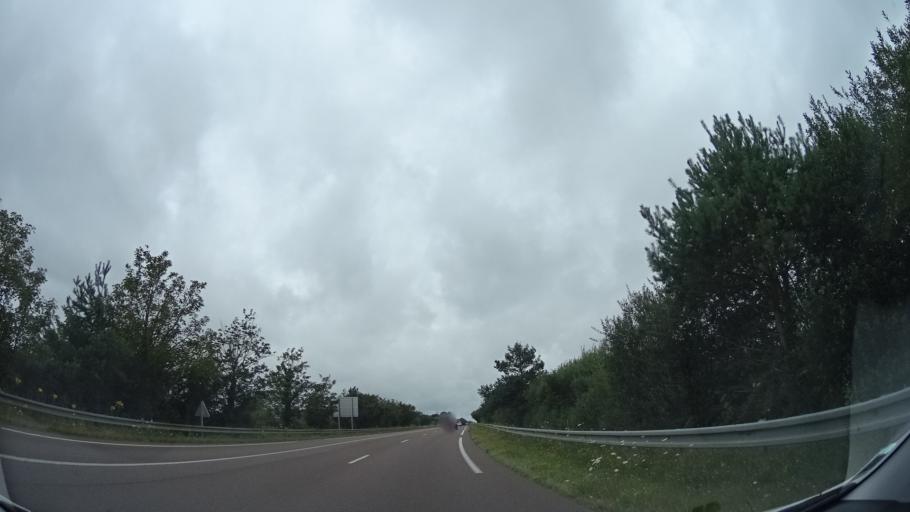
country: FR
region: Lower Normandy
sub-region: Departement de la Manche
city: La Haye-du-Puits
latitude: 49.2796
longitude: -1.5432
